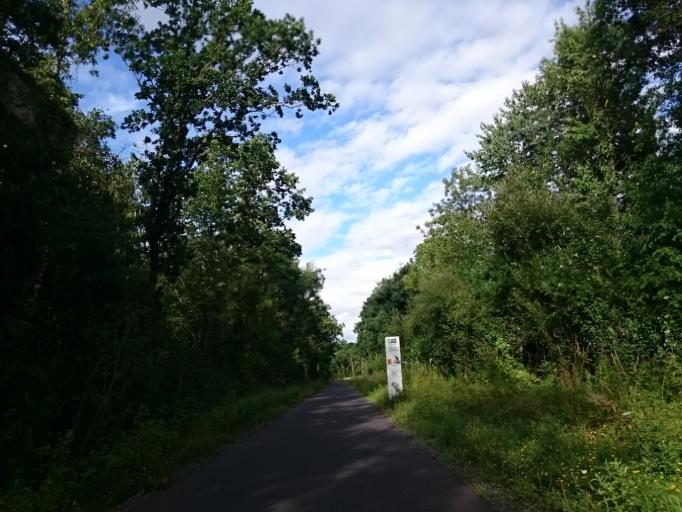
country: FR
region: Lower Normandy
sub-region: Departement du Calvados
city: Bully
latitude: 49.0986
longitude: -0.3934
